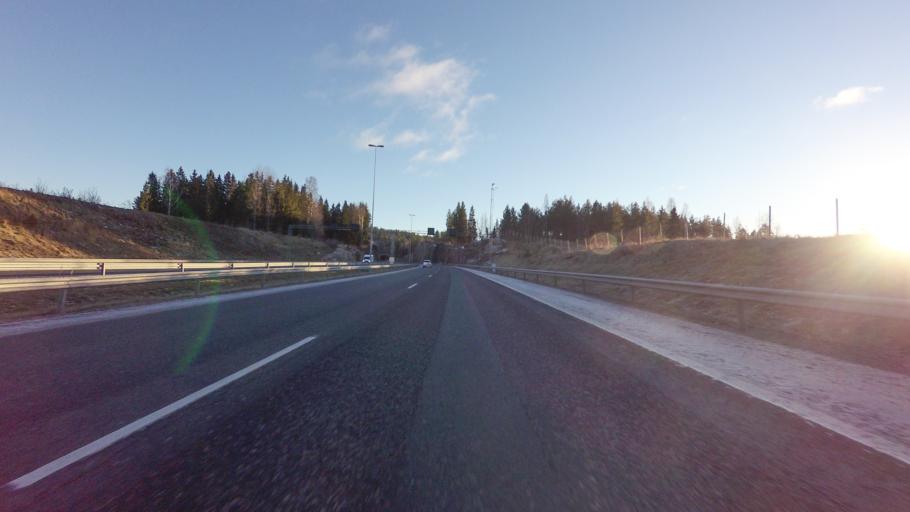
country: FI
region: Uusimaa
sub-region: Helsinki
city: Saukkola
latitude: 60.3287
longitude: 23.9354
